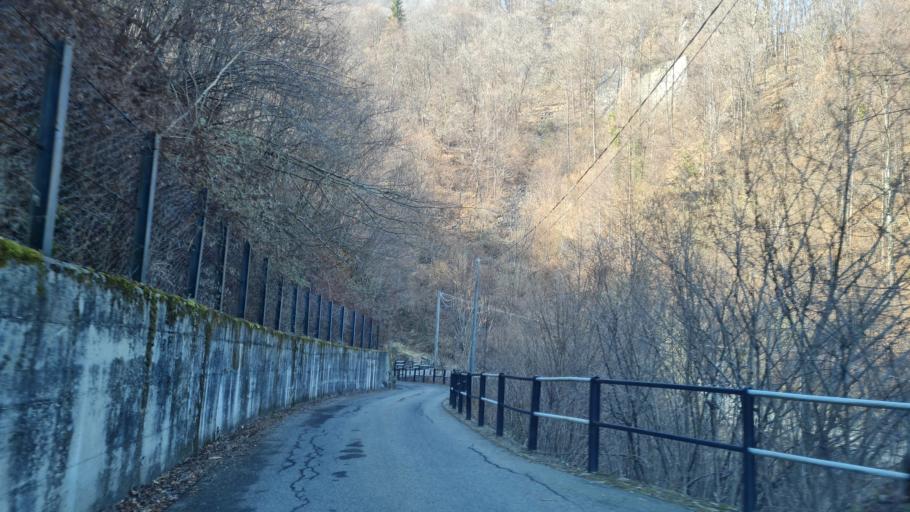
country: IT
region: Piedmont
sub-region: Provincia di Biella
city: San Paolo Cervo
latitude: 45.6414
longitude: 8.0173
